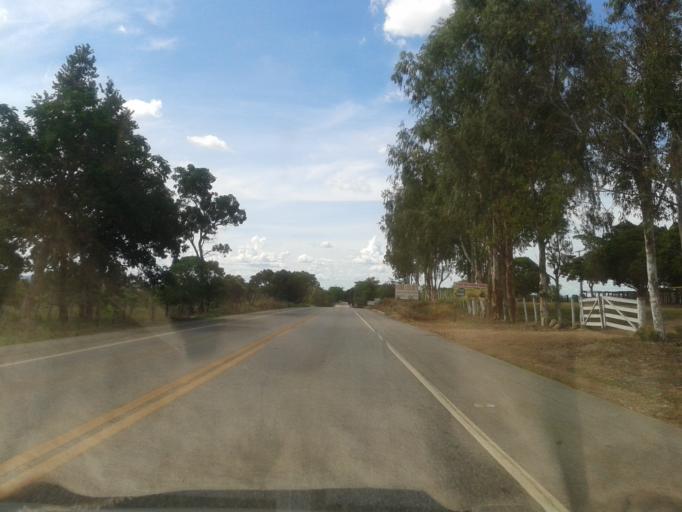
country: BR
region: Goias
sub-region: Itapuranga
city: Itapuranga
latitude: -15.4644
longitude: -50.3530
